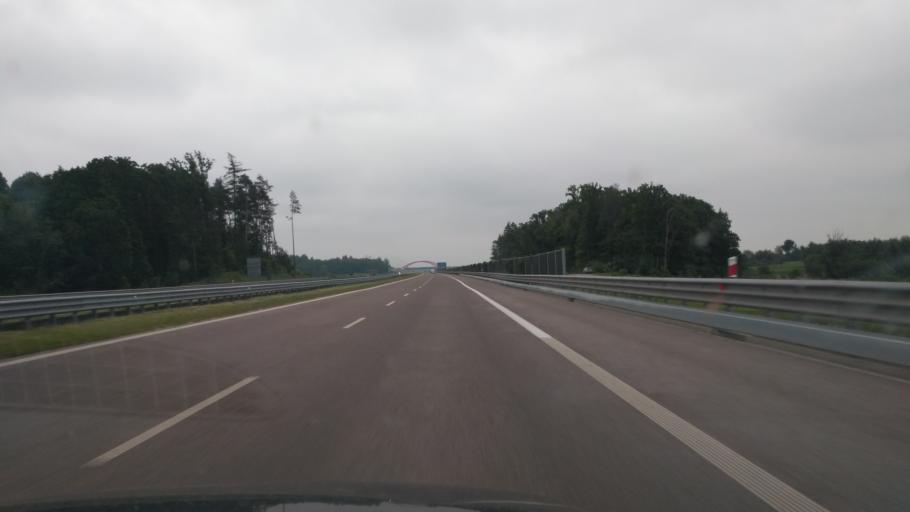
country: PL
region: Subcarpathian Voivodeship
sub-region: Powiat jaroslawski
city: Pawlosiow
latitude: 49.9789
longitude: 22.6295
